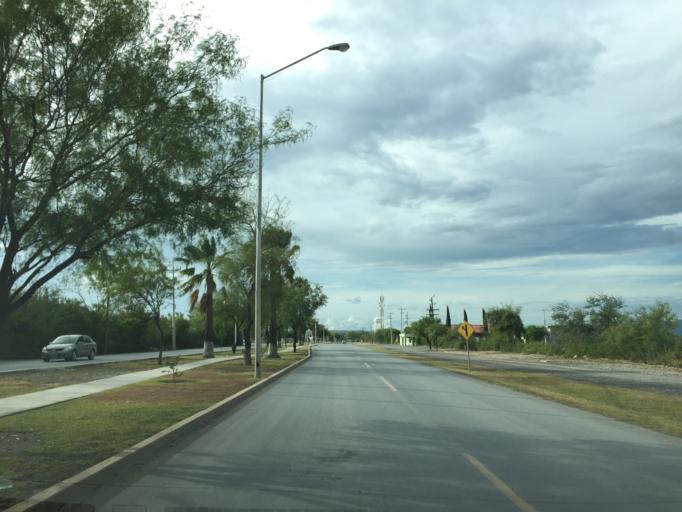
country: MX
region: Nuevo Leon
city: Marin
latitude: 25.8672
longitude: -100.0254
